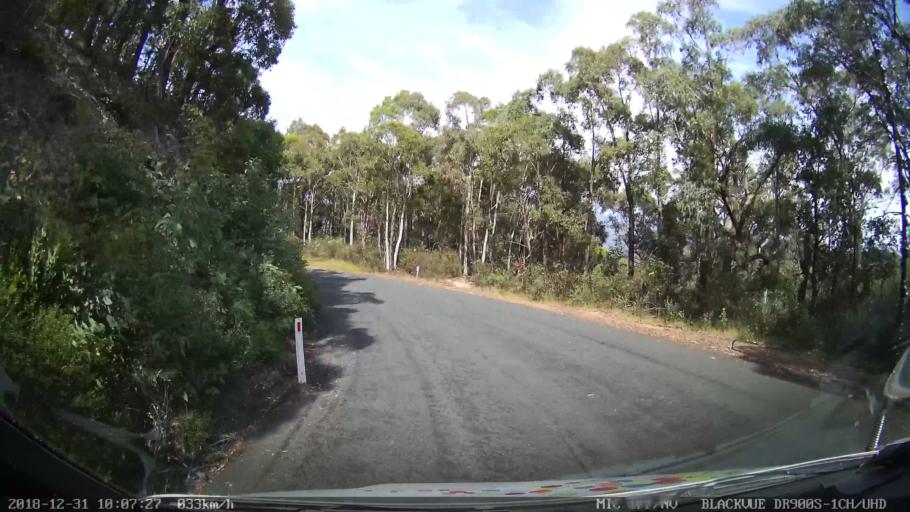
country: AU
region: New South Wales
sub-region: Snowy River
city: Jindabyne
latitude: -36.5315
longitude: 148.1835
